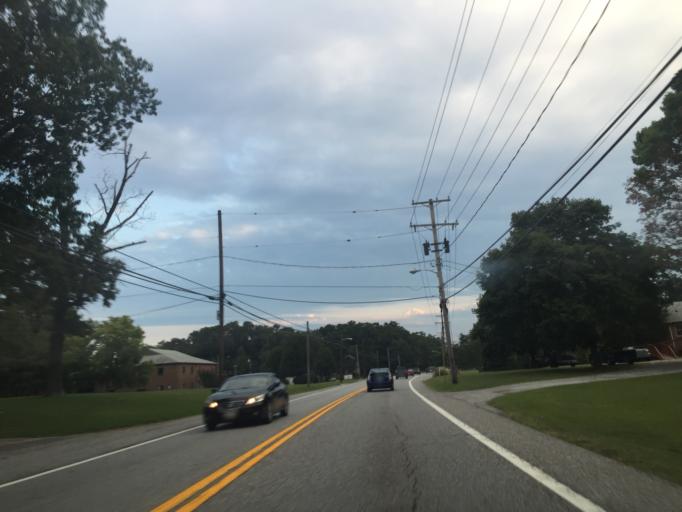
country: US
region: Maryland
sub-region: Anne Arundel County
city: Severn
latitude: 39.1259
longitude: -76.6892
